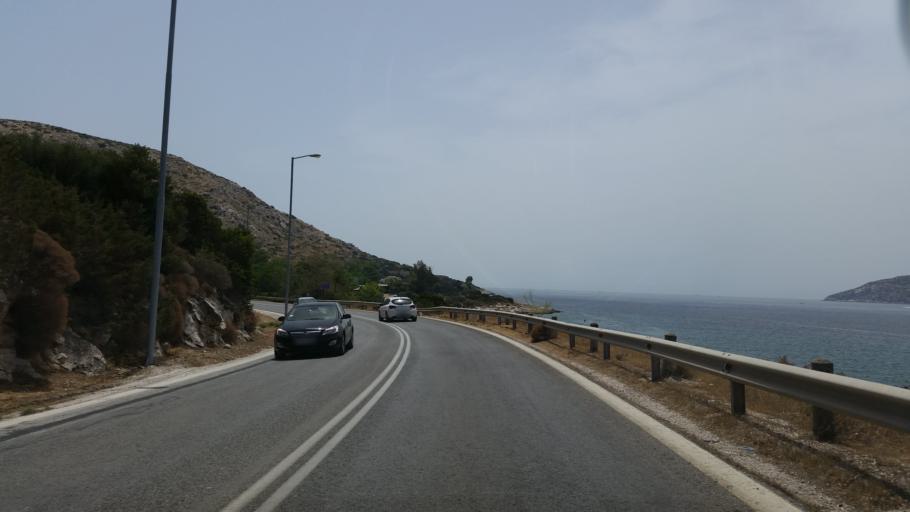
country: GR
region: Attica
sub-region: Nomarchia Anatolikis Attikis
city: Palaia Fokaia
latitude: 37.7135
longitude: 23.9434
